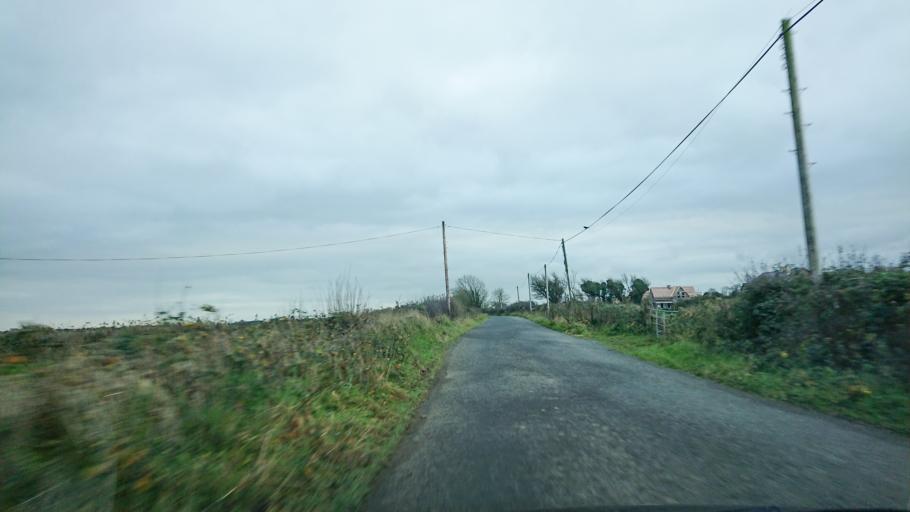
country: IE
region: Munster
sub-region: Waterford
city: Dunmore East
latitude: 52.2407
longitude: -6.9945
